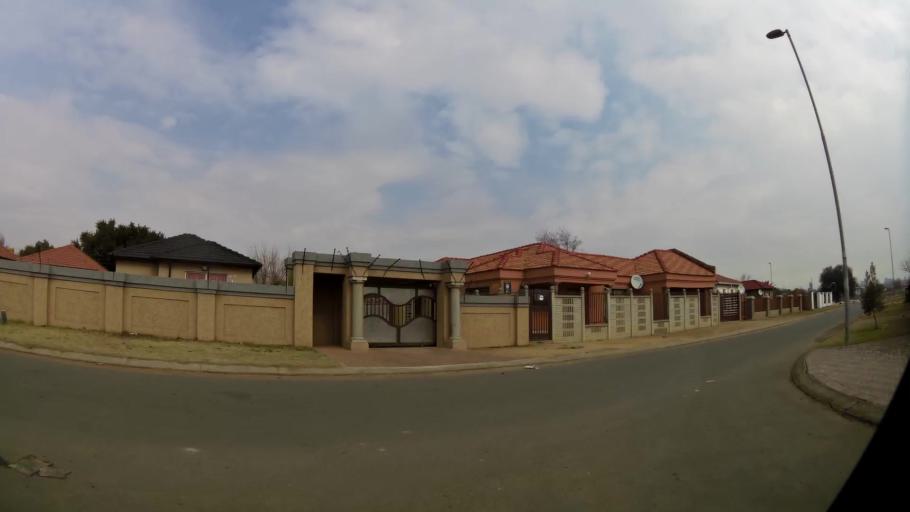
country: ZA
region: Gauteng
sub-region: Sedibeng District Municipality
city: Vanderbijlpark
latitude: -26.6848
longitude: 27.8423
